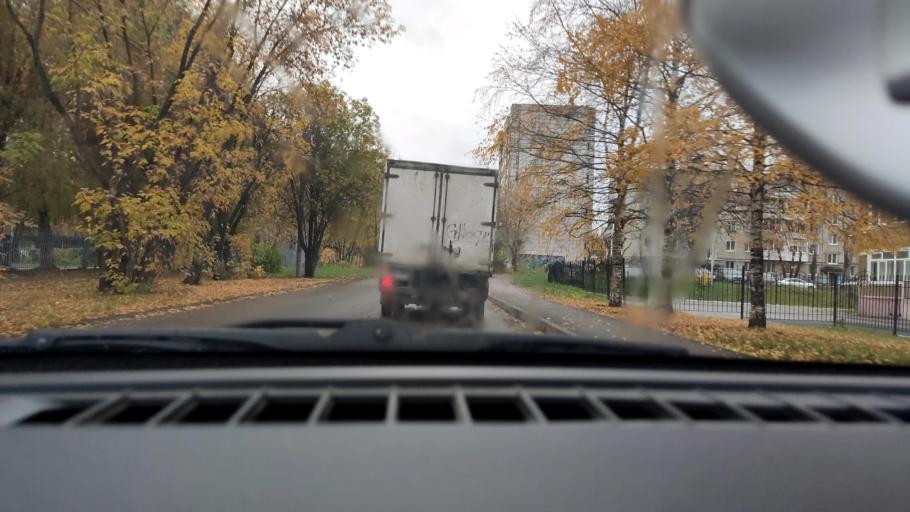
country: RU
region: Perm
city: Perm
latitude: 57.9874
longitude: 56.2239
